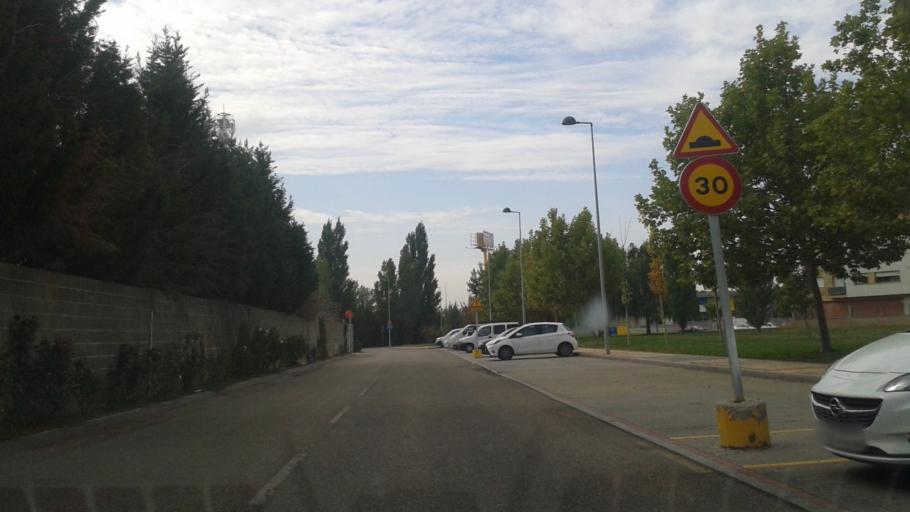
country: ES
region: Castille and Leon
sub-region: Provincia de Valladolid
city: Arroyo
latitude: 41.6186
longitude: -4.7749
